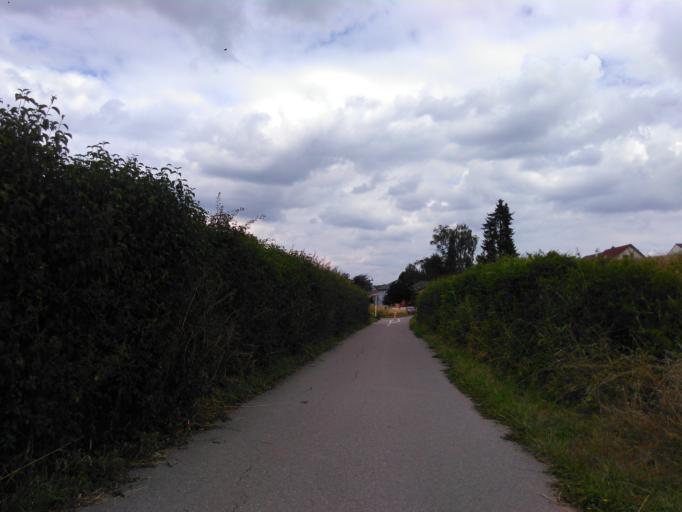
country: LU
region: Grevenmacher
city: Gonderange
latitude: 49.6896
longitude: 6.2504
